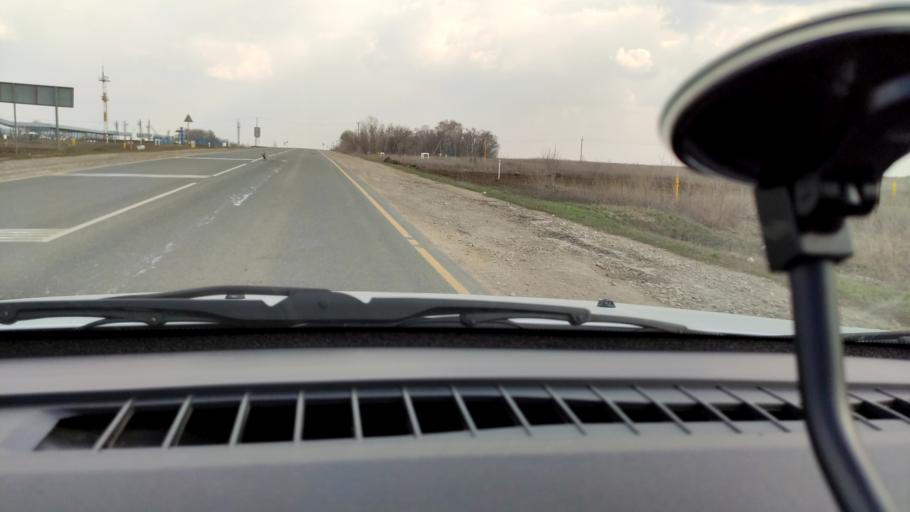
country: RU
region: Samara
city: Dubovyy Umet
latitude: 53.0828
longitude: 50.3446
